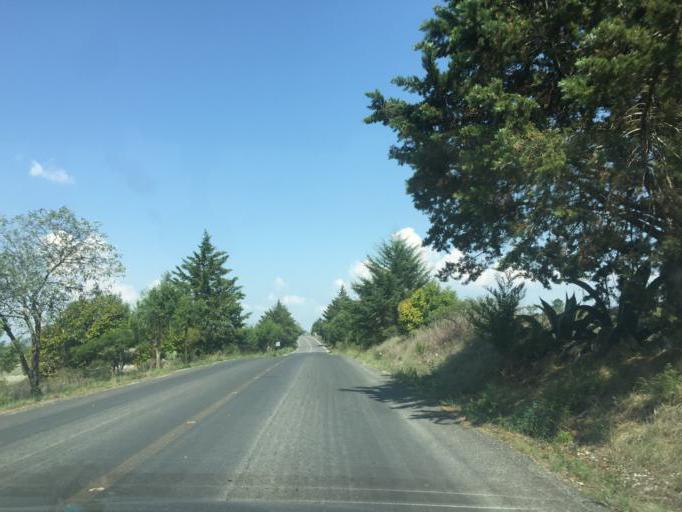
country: MX
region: Hidalgo
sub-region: Cardonal
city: Pozuelos
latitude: 20.6149
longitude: -99.0594
